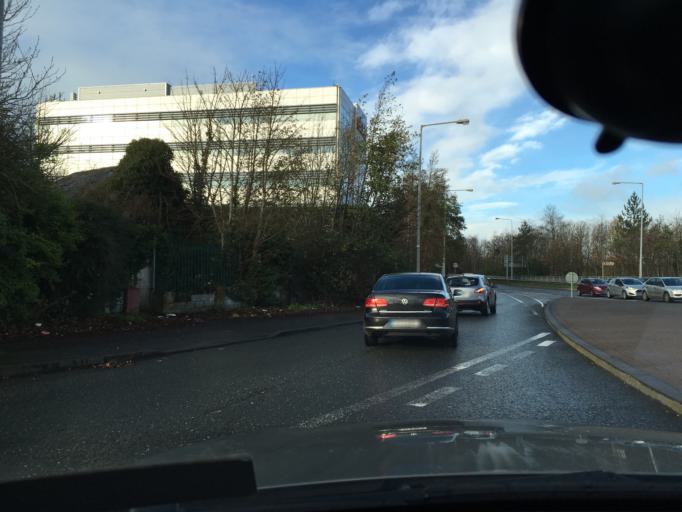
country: IE
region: Leinster
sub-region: Fingal County
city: Blanchardstown
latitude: 53.3916
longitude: -6.3822
